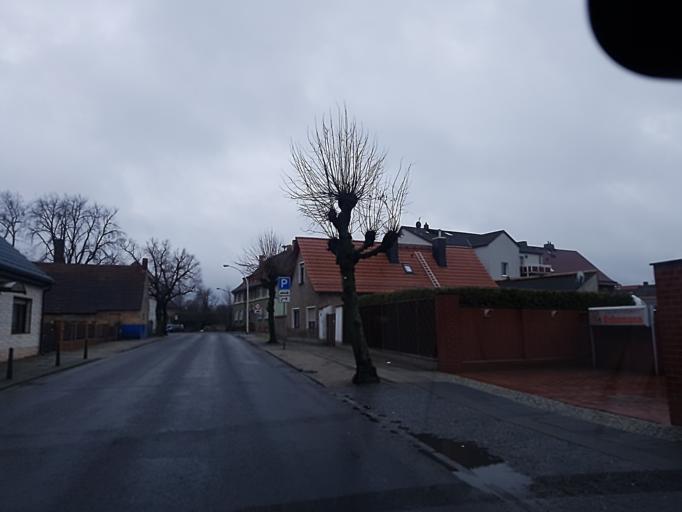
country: DE
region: Brandenburg
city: Finsterwalde
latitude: 51.6153
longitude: 13.7141
